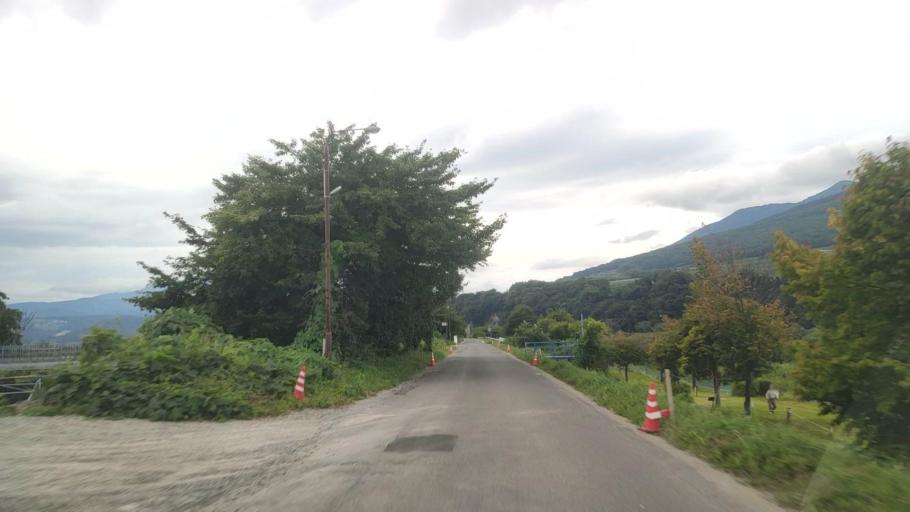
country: JP
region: Nagano
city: Nakano
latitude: 36.7653
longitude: 138.3939
